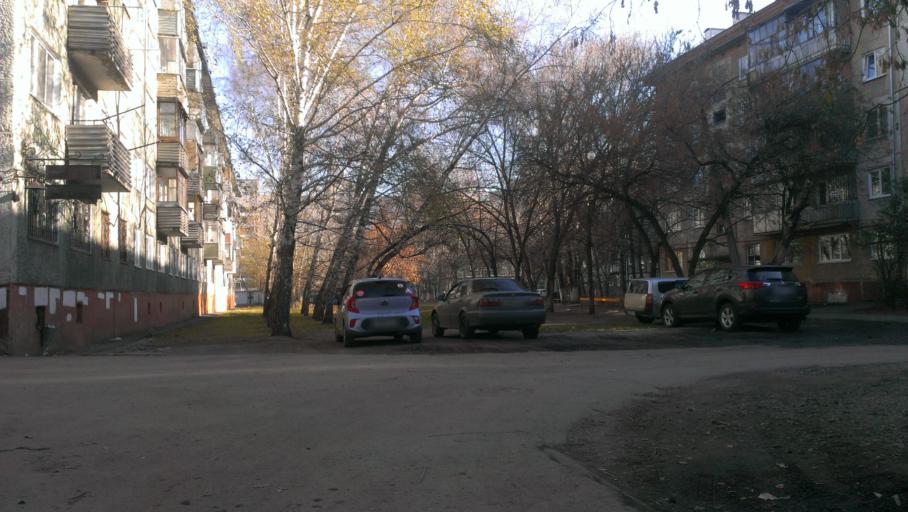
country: RU
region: Altai Krai
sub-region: Gorod Barnaulskiy
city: Barnaul
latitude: 53.3444
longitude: 83.6916
